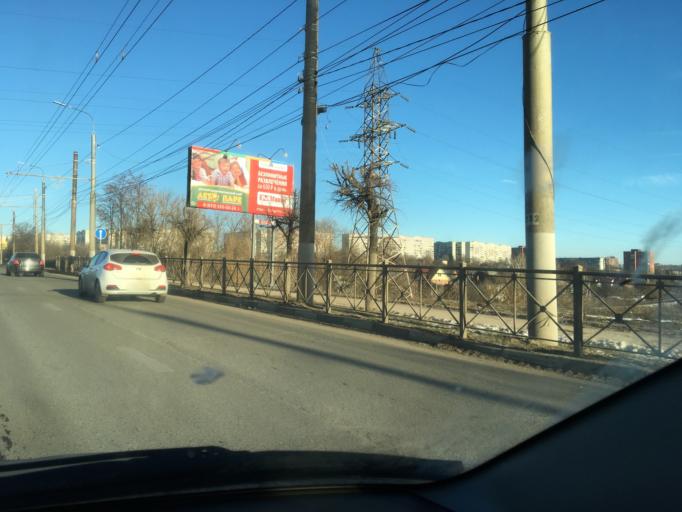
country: RU
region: Tula
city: Tula
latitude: 54.1953
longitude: 37.6321
